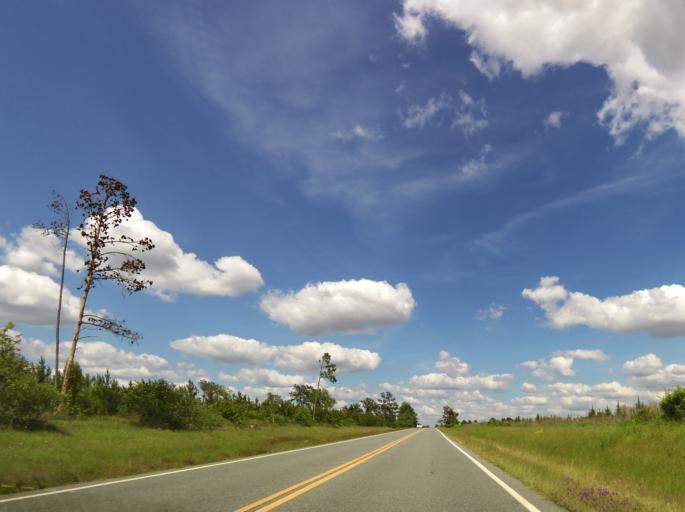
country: US
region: Georgia
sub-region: Telfair County
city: Helena
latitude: 32.2306
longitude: -82.9783
